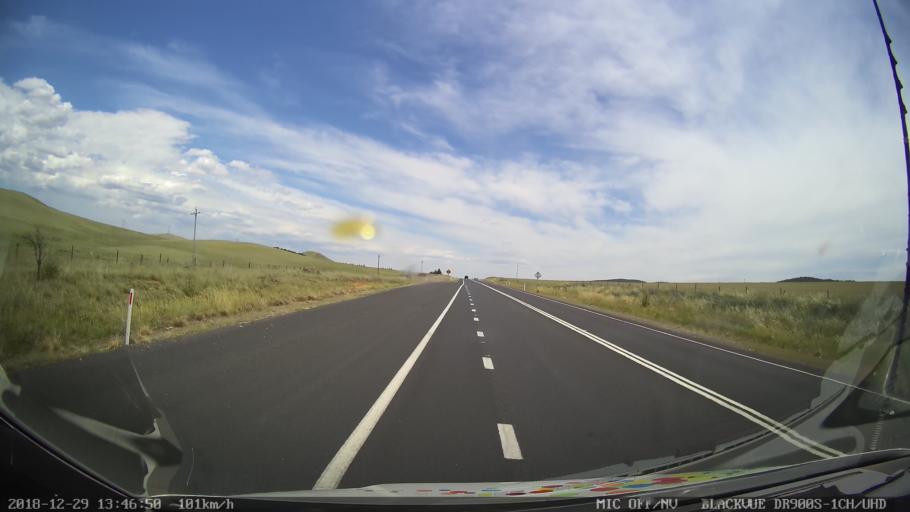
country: AU
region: New South Wales
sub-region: Cooma-Monaro
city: Cooma
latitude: -36.1172
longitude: 149.1417
